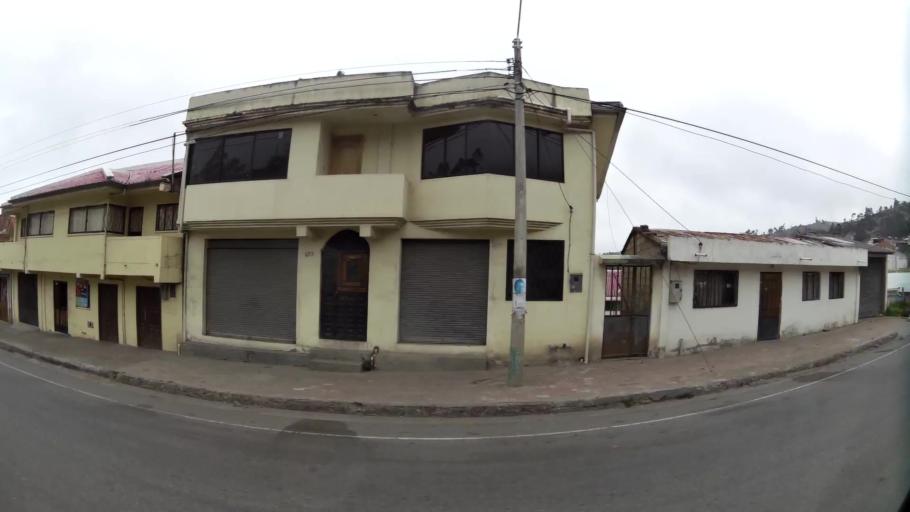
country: EC
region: Canar
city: Canar
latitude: -2.5048
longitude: -78.9251
